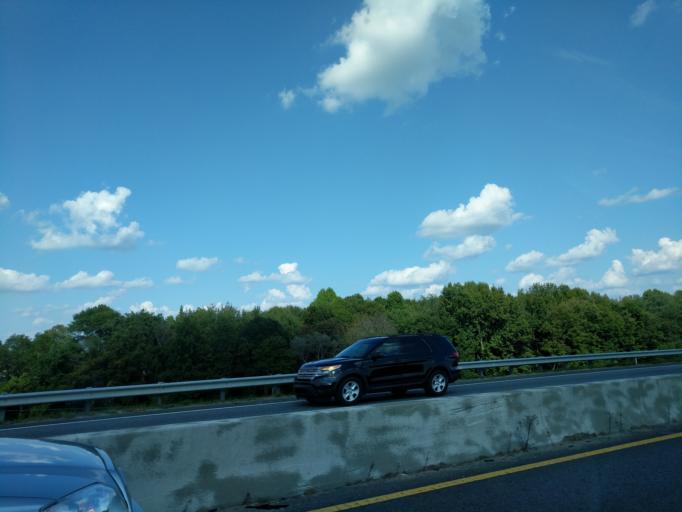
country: US
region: South Carolina
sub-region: Greenville County
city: Fountain Inn
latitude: 34.6684
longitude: -82.1811
